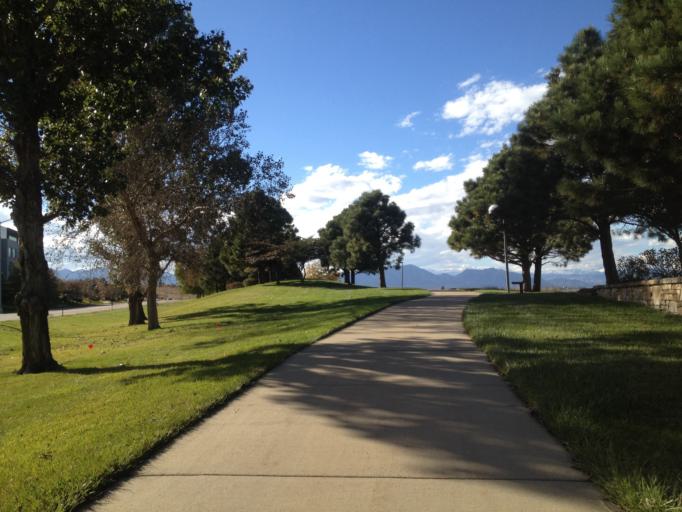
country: US
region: Colorado
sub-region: Broomfield County
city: Broomfield
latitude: 39.9168
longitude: -105.1159
